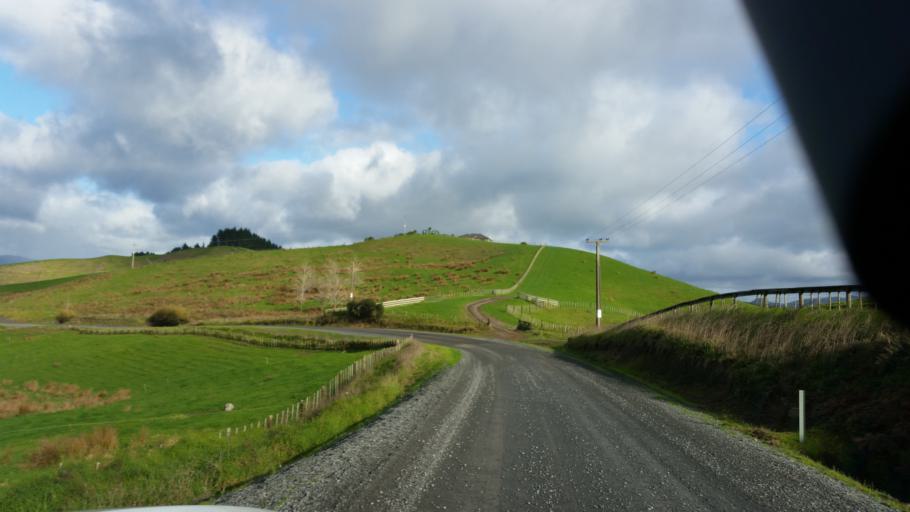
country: NZ
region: Northland
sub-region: Whangarei
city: Maungatapere
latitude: -35.7034
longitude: 174.0874
